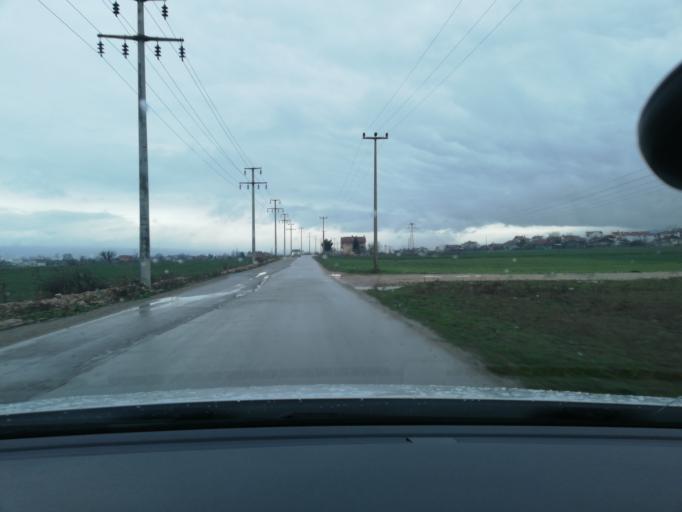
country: TR
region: Bolu
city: Bolu
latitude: 40.7583
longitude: 31.6416
